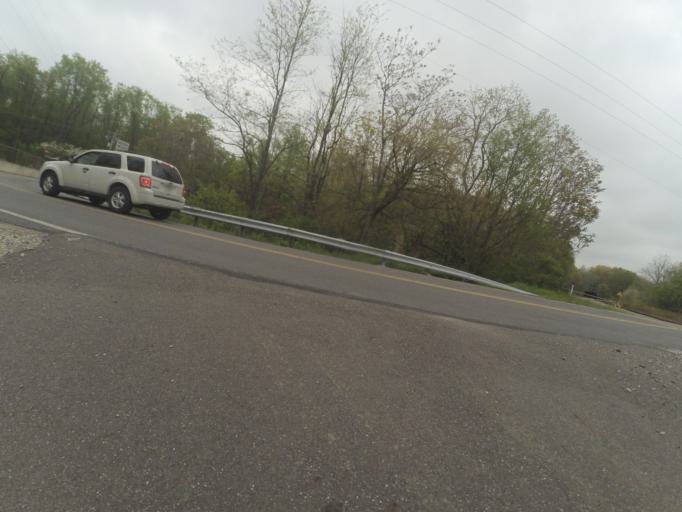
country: US
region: Ohio
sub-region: Portage County
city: Kent
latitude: 41.1719
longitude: -81.3129
